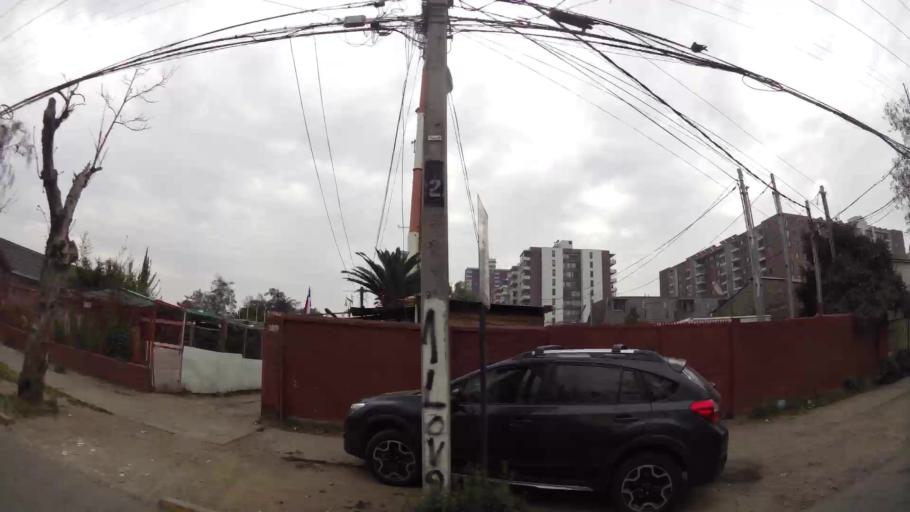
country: CL
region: Santiago Metropolitan
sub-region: Provincia de Santiago
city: Villa Presidente Frei, Nunoa, Santiago, Chile
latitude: -33.4801
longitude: -70.5965
